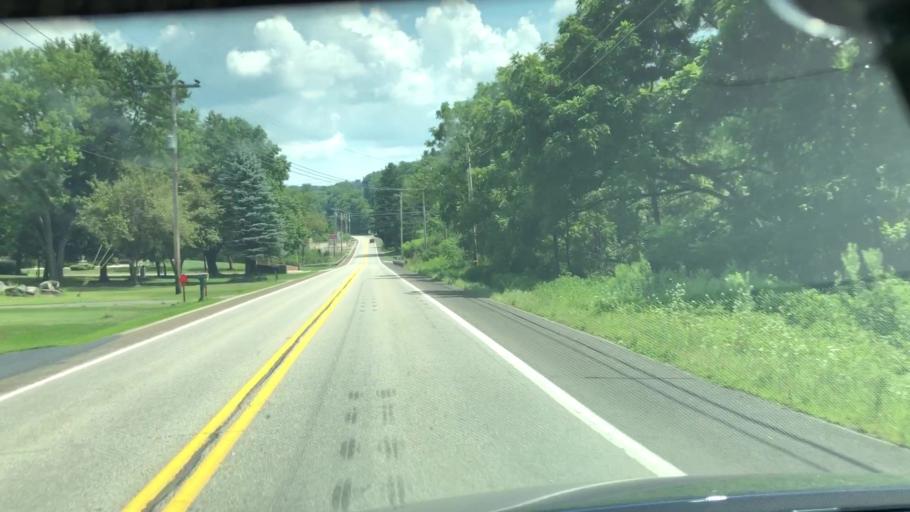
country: US
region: Pennsylvania
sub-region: Butler County
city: Saxonburg
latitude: 40.7142
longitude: -79.7484
